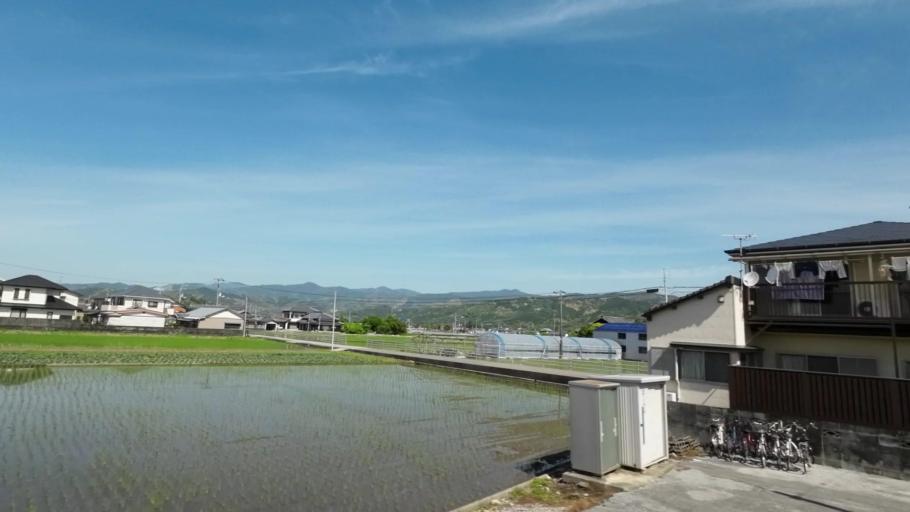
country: JP
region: Kochi
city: Kochi-shi
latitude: 33.6050
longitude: 133.6778
